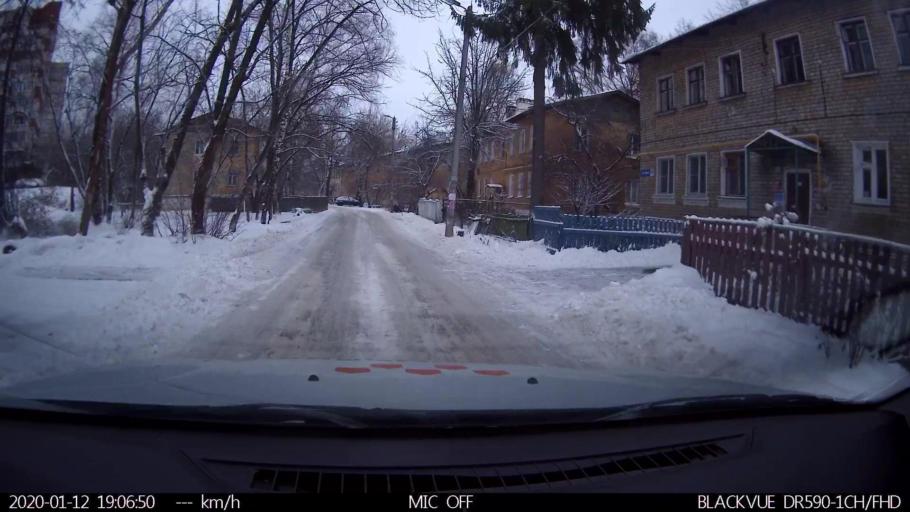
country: RU
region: Nizjnij Novgorod
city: Nizhniy Novgorod
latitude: 56.3328
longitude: 43.9112
